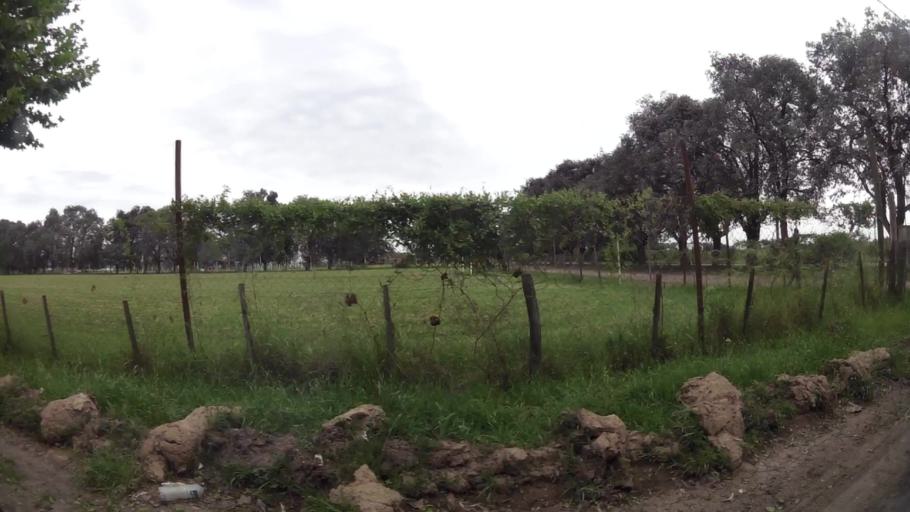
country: AR
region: Buenos Aires
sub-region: Partido de Campana
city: Campana
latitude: -34.2009
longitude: -58.9488
